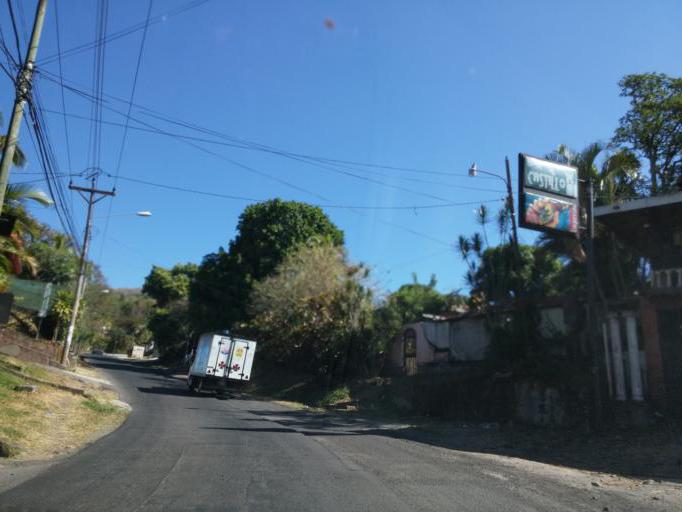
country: CR
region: Alajuela
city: Sabanilla
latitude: 10.0459
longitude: -84.2093
